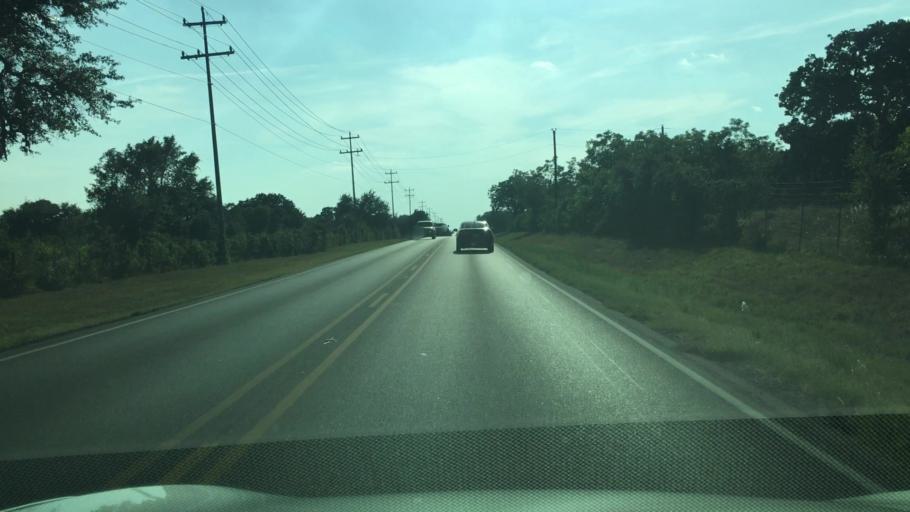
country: US
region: Texas
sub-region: Travis County
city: Shady Hollow
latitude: 30.1174
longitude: -97.9621
